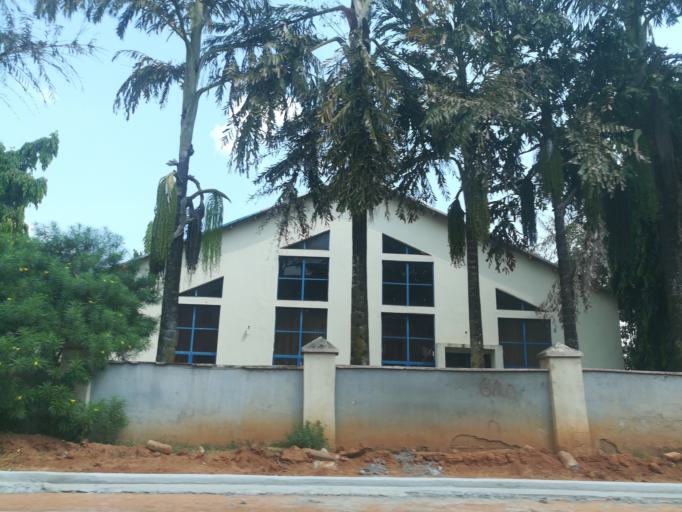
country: NG
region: Abuja Federal Capital Territory
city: Abuja
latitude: 9.0515
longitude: 7.4472
